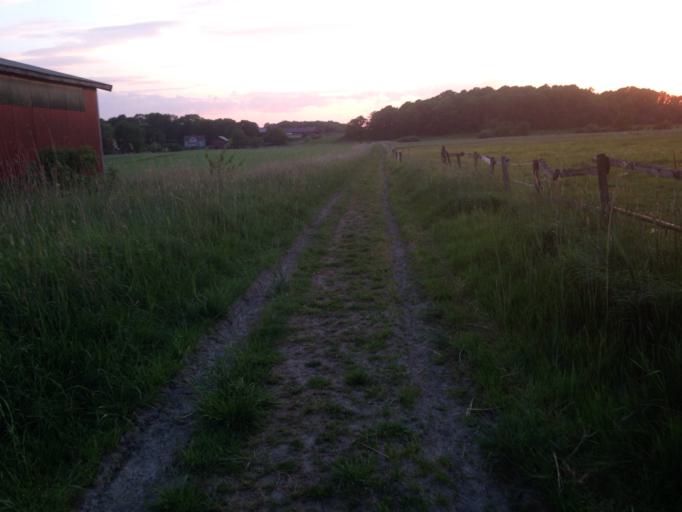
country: SE
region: Vaestra Goetaland
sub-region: Goteborg
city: Majorna
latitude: 57.7934
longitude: 11.8773
